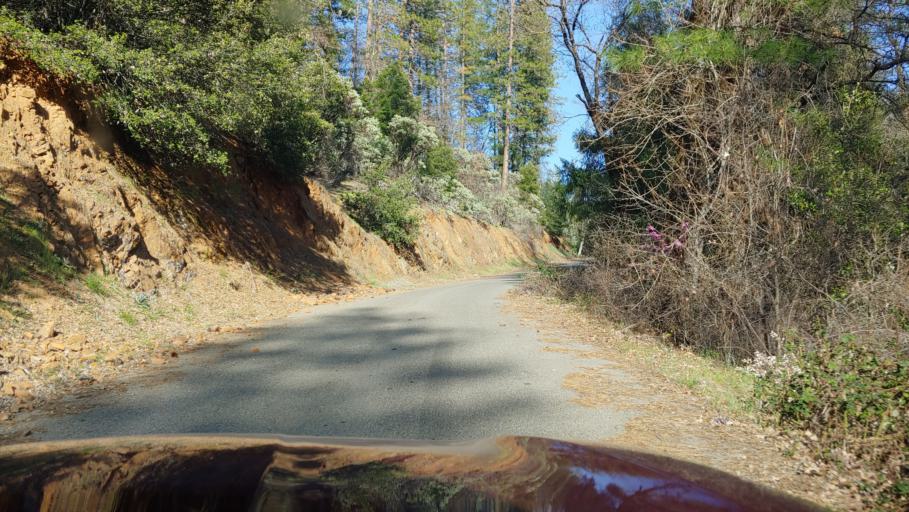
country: US
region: California
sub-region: Siskiyou County
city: Dunsmuir
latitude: 40.9971
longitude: -122.4128
